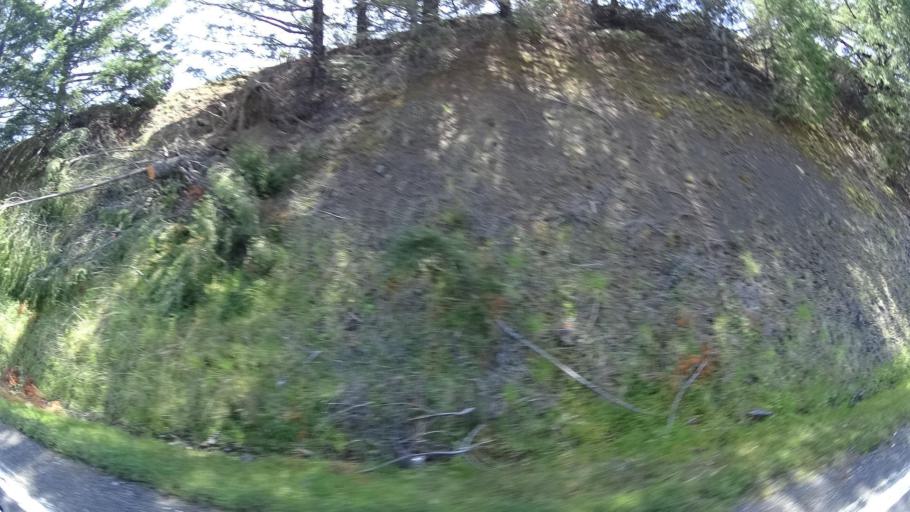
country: US
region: California
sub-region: Humboldt County
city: Redway
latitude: 40.1003
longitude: -123.6847
